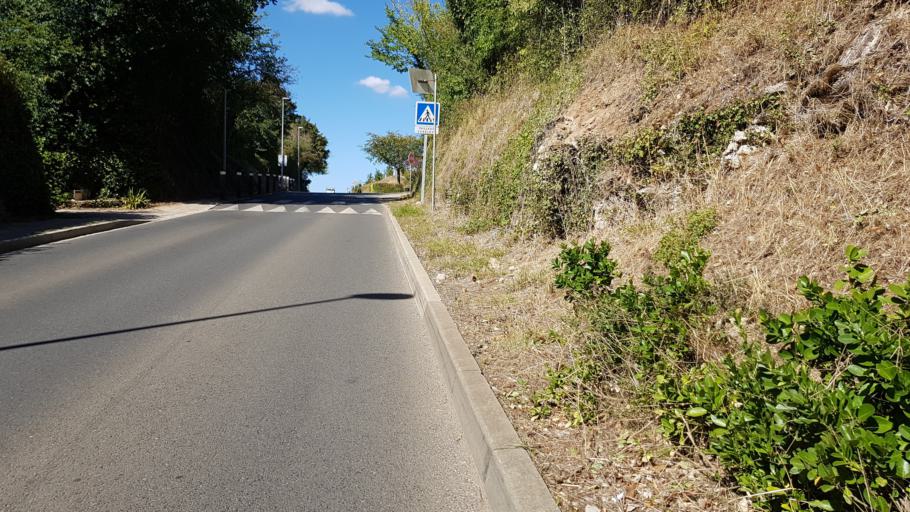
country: FR
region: Poitou-Charentes
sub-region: Departement des Deux-Sevres
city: Vouille
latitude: 46.3204
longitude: -0.3703
